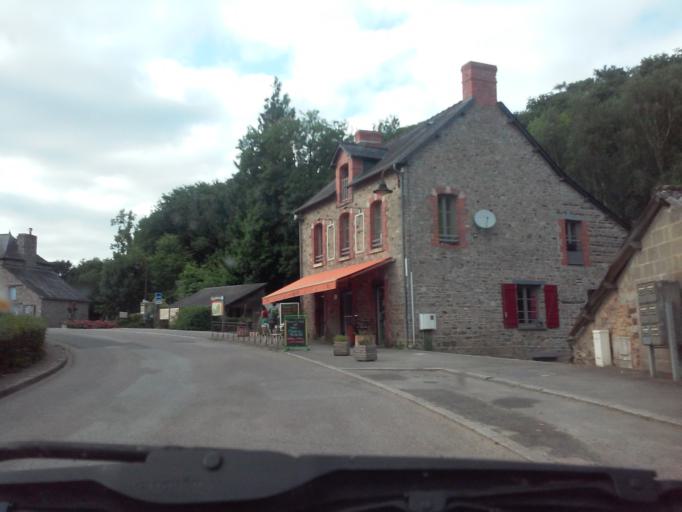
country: FR
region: Brittany
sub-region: Departement d'Ille-et-Vilaine
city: Saint-Senoux
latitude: 47.9049
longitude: -1.7872
